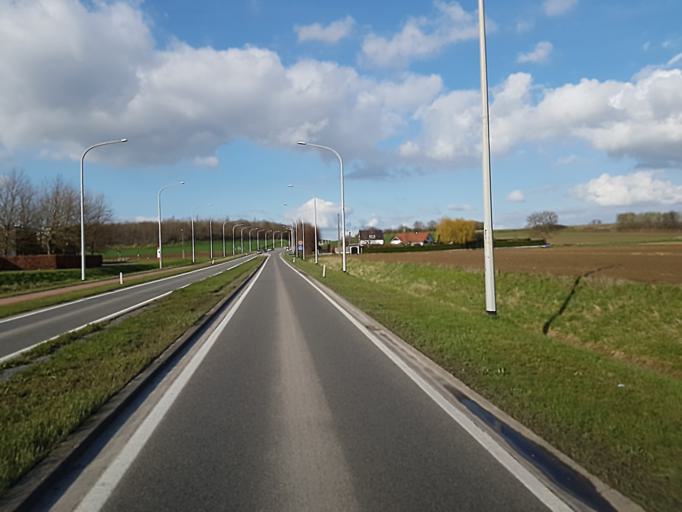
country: BE
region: Flanders
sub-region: Provincie Vlaams-Brabant
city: Hoegaarden
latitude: 50.7718
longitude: 4.9110
